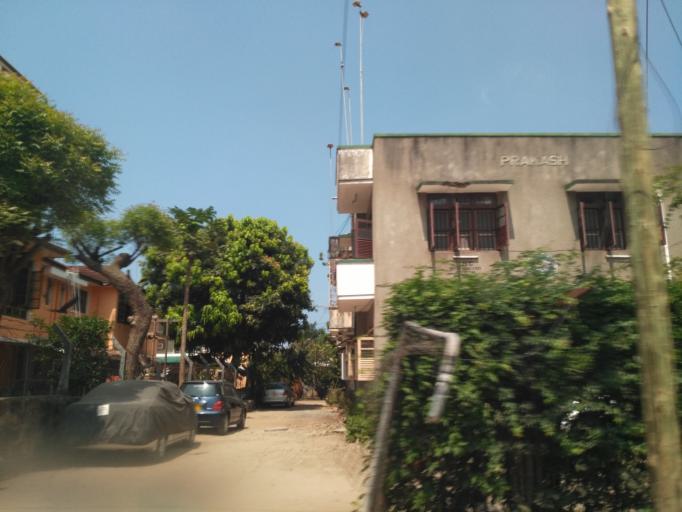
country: TZ
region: Dar es Salaam
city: Dar es Salaam
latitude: -6.8062
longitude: 39.2842
